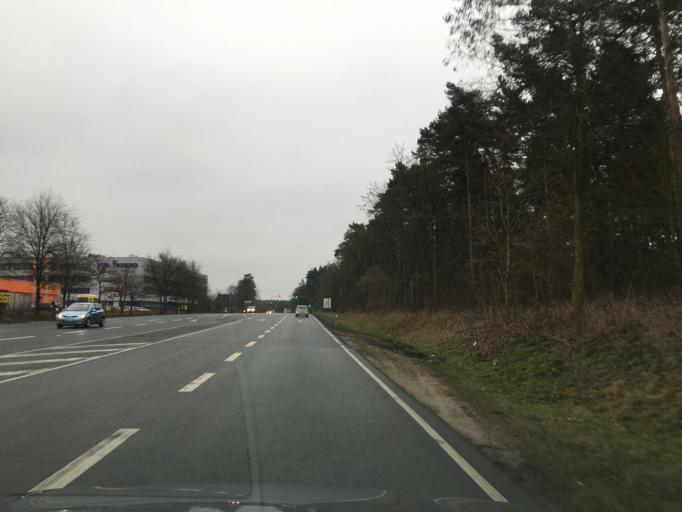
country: DE
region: Bavaria
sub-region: Regierungsbezirk Mittelfranken
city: Neunkirchen am Sand
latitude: 49.5169
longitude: 11.3095
